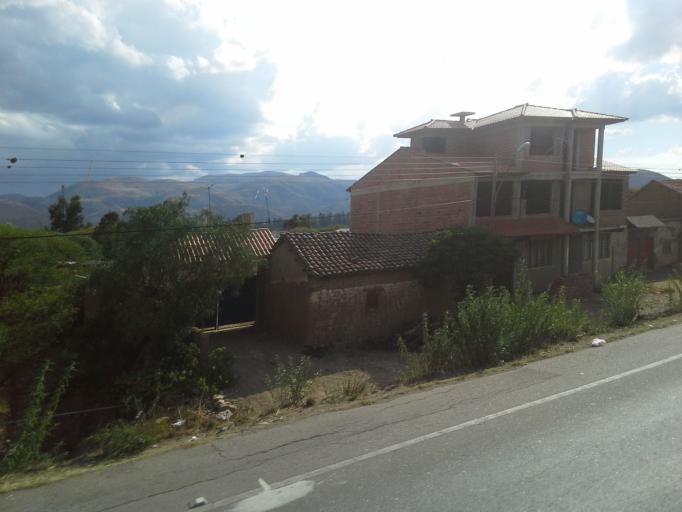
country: BO
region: Cochabamba
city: Tarata
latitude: -17.5367
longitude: -66.0761
